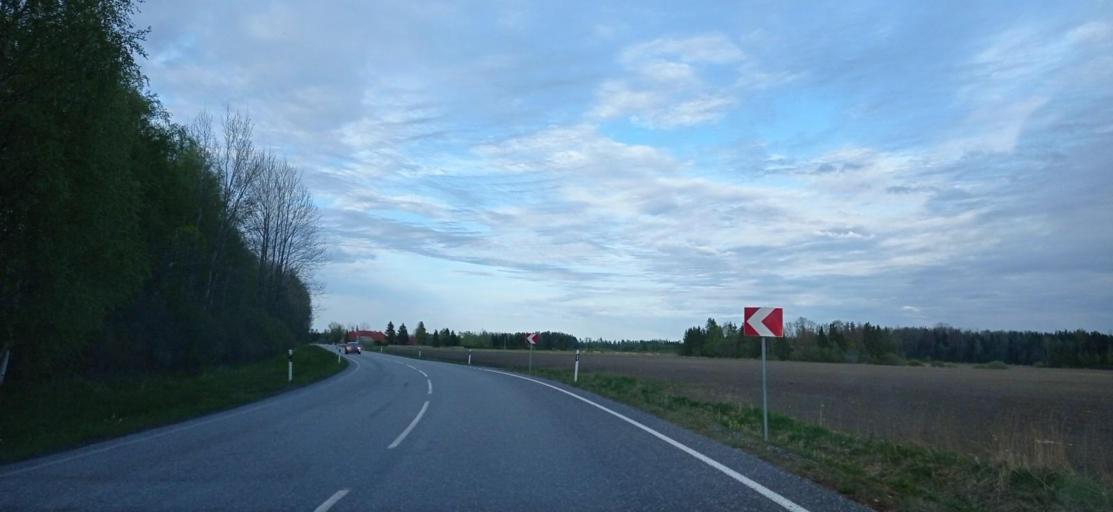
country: EE
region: Paernumaa
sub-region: Sindi linn
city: Sindi
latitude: 58.5224
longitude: 24.6402
